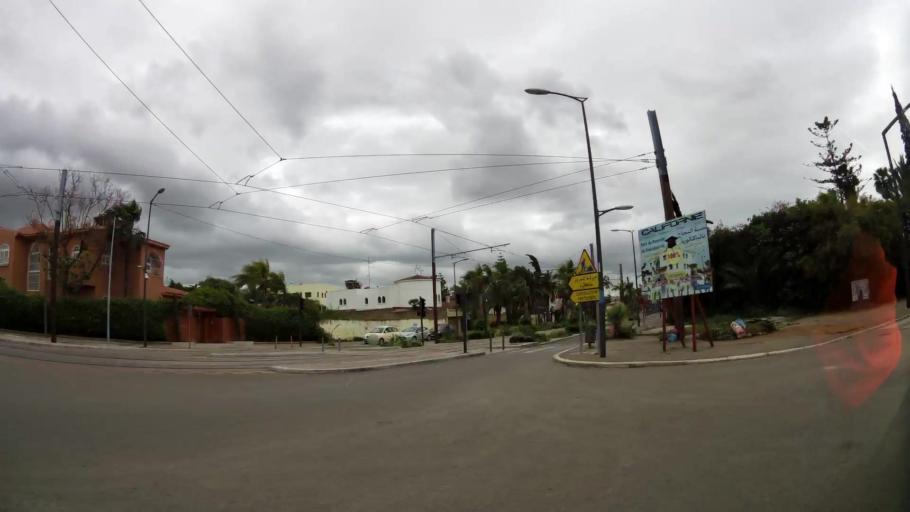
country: MA
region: Grand Casablanca
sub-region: Casablanca
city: Casablanca
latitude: 33.5459
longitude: -7.6376
